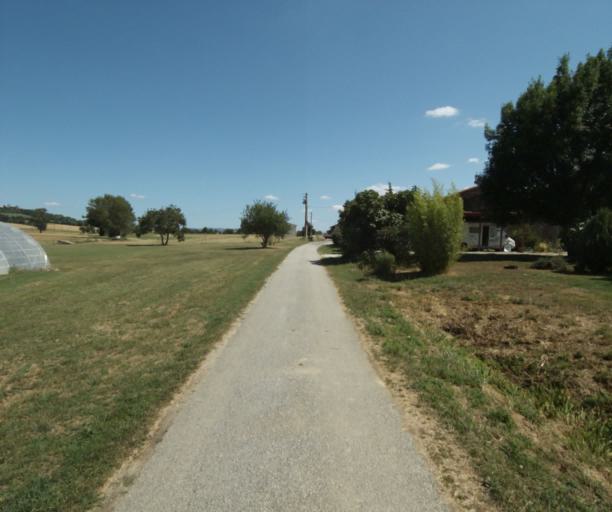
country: FR
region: Midi-Pyrenees
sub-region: Departement de la Haute-Garonne
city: Saint-Felix-Lauragais
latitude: 43.4900
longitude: 1.8745
